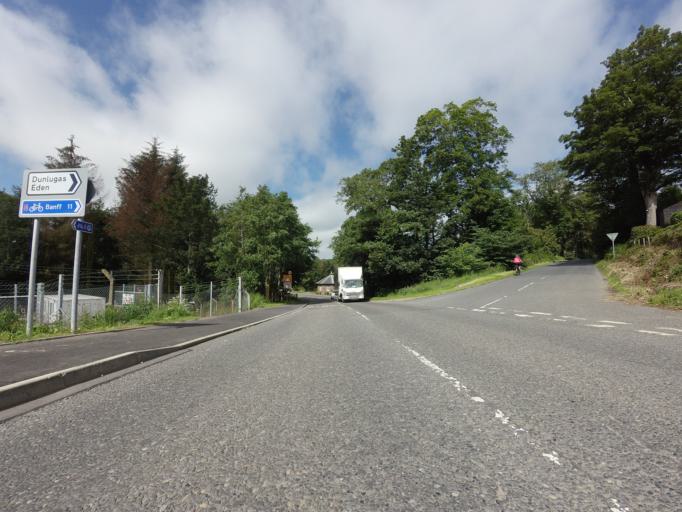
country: GB
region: Scotland
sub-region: Aberdeenshire
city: Turriff
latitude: 57.5425
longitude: -2.4773
